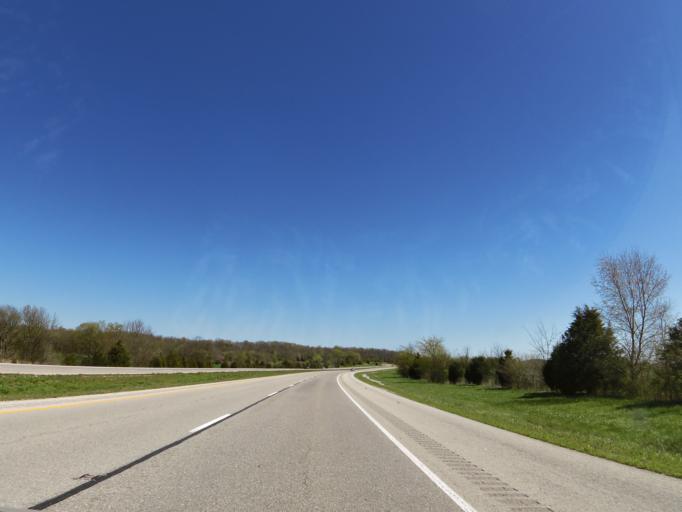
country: US
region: Kentucky
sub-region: Logan County
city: Auburn
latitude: 36.8650
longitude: -86.7345
